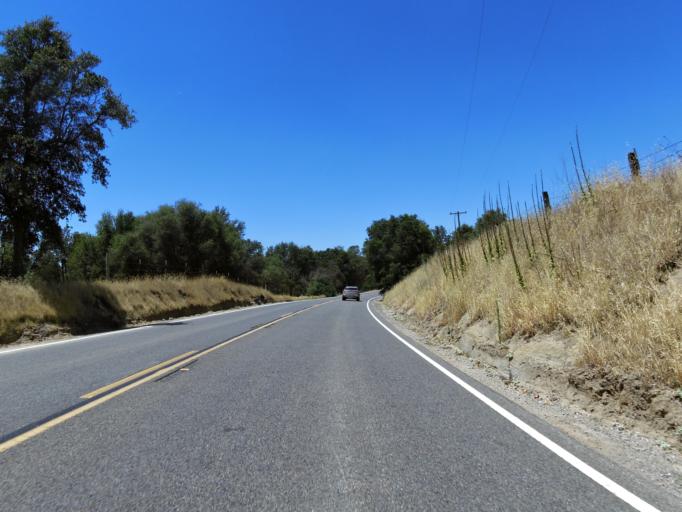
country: US
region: California
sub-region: Fresno County
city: Auberry
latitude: 37.0428
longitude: -119.4948
